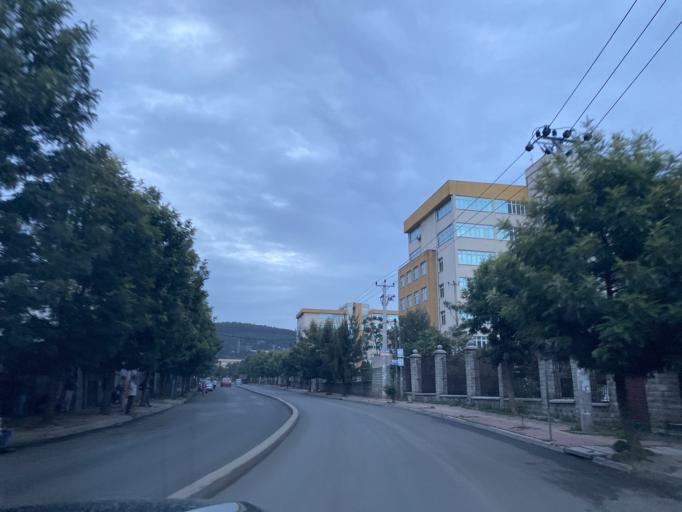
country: ET
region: Adis Abeba
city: Addis Ababa
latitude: 9.0147
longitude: 38.8115
